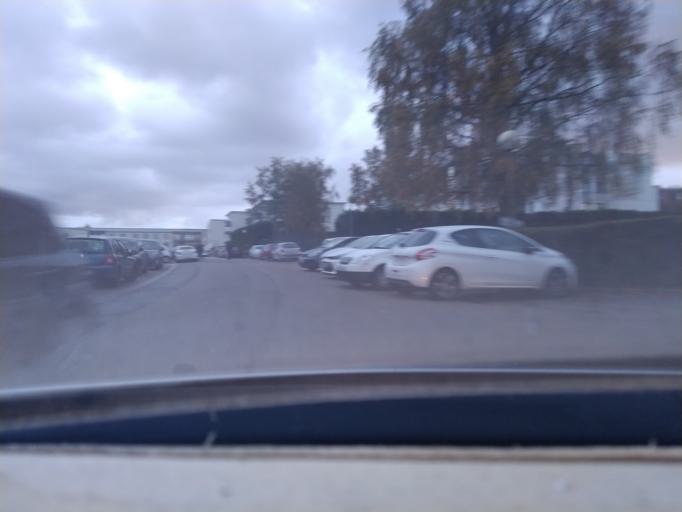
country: FR
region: Haute-Normandie
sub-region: Departement de la Seine-Maritime
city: Canteleu
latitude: 49.4433
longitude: 1.0169
